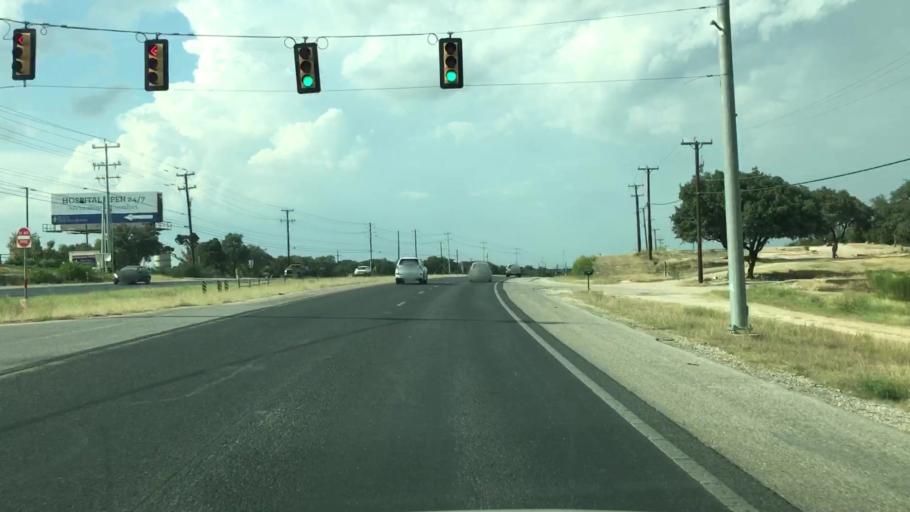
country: US
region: Texas
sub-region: Bexar County
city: Timberwood Park
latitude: 29.6804
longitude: -98.4525
